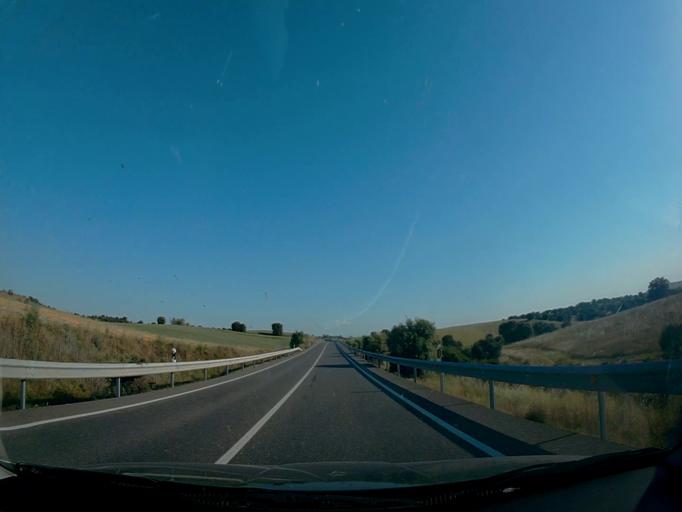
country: ES
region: Castille-La Mancha
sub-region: Province of Toledo
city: Almorox
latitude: 40.2079
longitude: -4.3970
